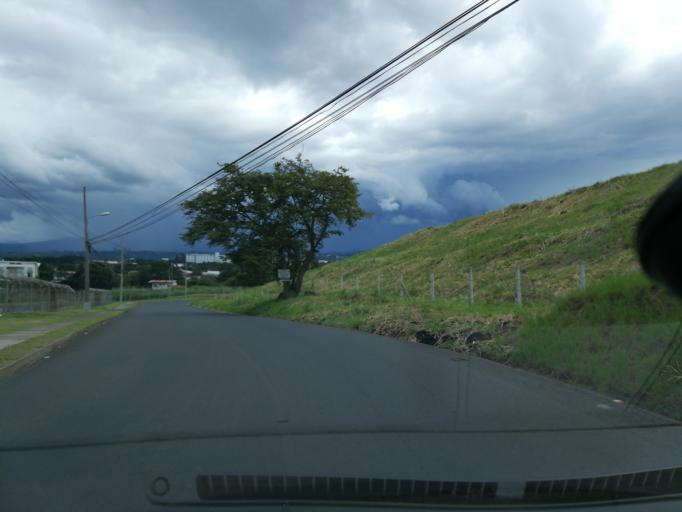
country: CR
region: Alajuela
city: Alajuela
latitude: 9.9968
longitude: -84.2151
